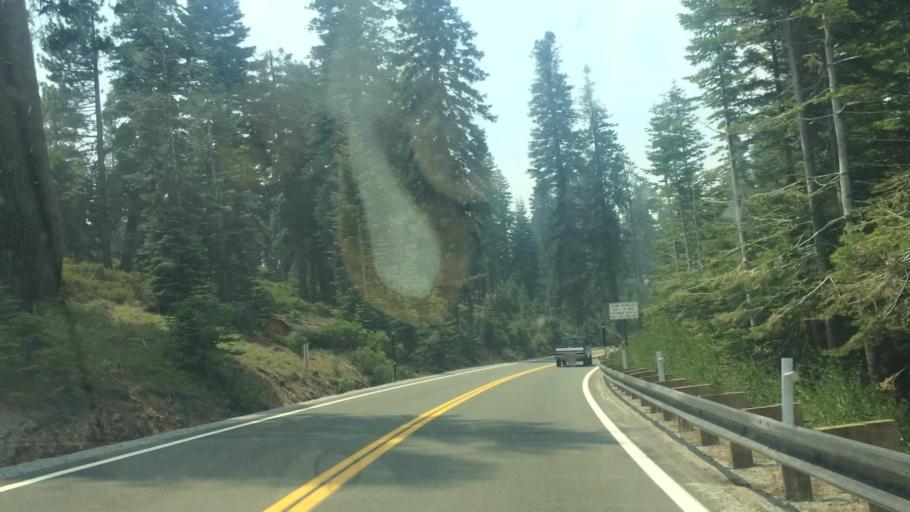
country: US
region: California
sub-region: Amador County
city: Pioneer
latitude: 38.5494
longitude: -120.3019
